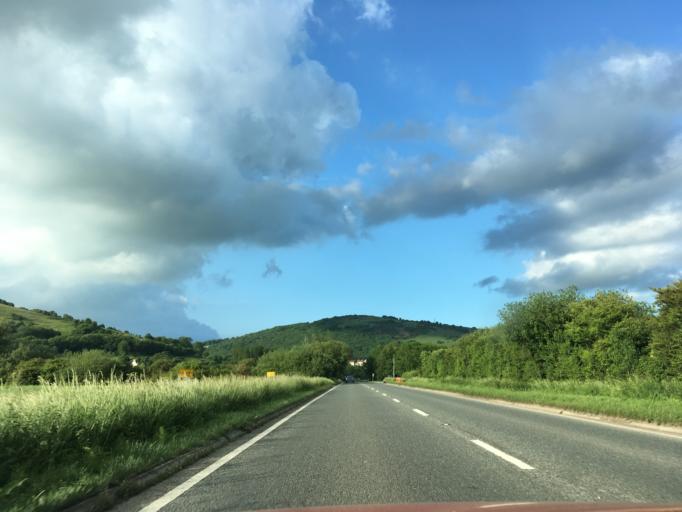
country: GB
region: England
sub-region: Somerset
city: Axbridge
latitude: 51.2839
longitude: -2.8435
